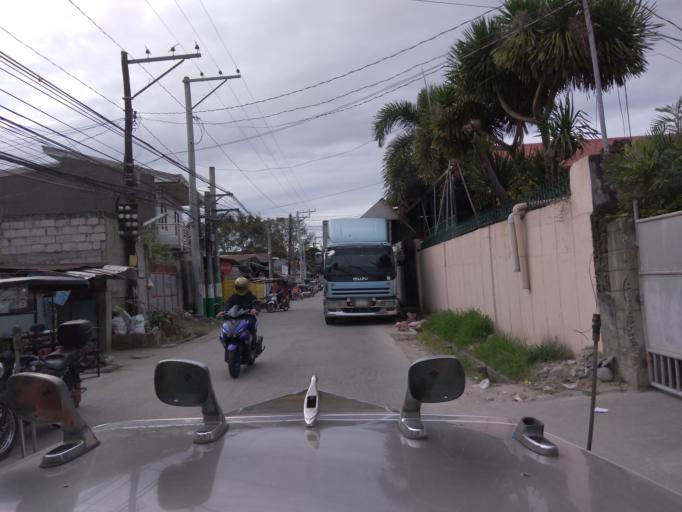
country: PH
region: Central Luzon
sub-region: Province of Pampanga
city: Mexico
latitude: 15.0641
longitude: 120.7230
